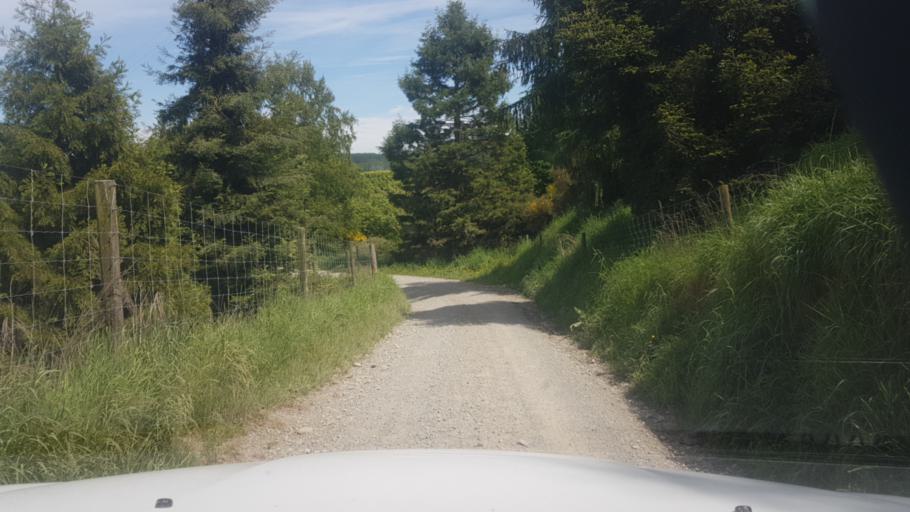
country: NZ
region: Canterbury
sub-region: Timaru District
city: Pleasant Point
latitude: -44.2210
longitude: 171.1246
